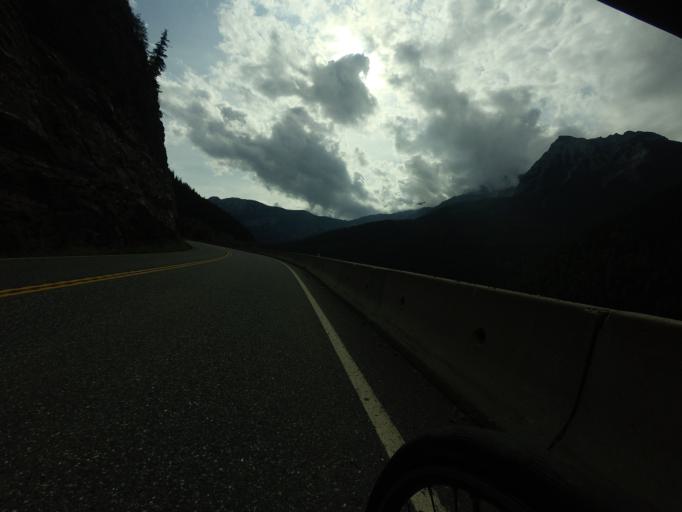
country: CA
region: British Columbia
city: Lillooet
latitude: 50.6415
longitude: -122.0388
